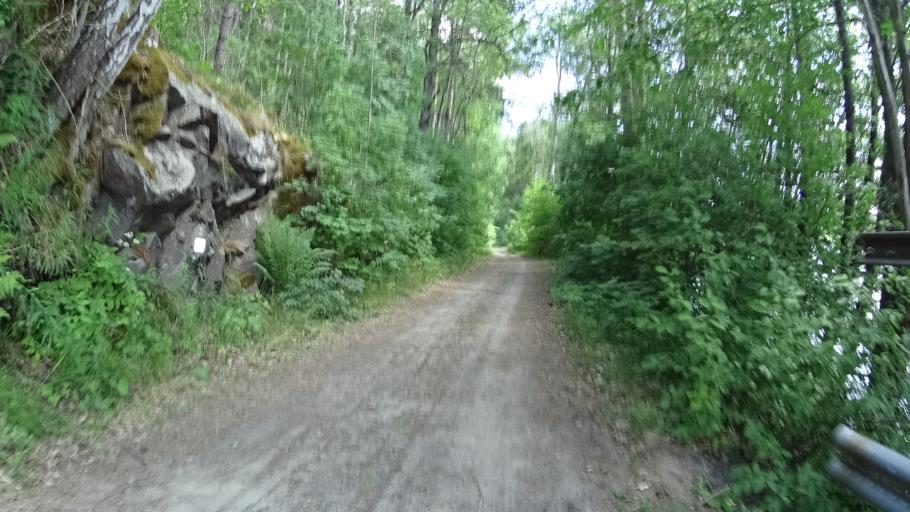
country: FI
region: Uusimaa
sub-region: Raaseporin
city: Pohja
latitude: 60.1117
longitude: 23.5453
